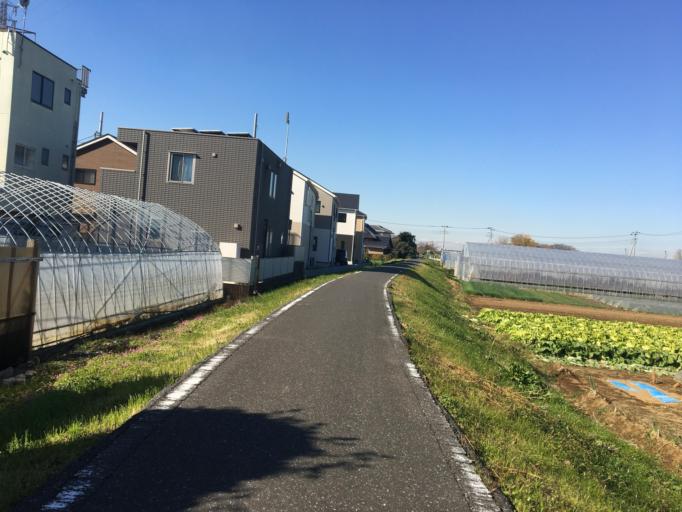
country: JP
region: Saitama
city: Yashio-shi
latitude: 35.8205
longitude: 139.8611
